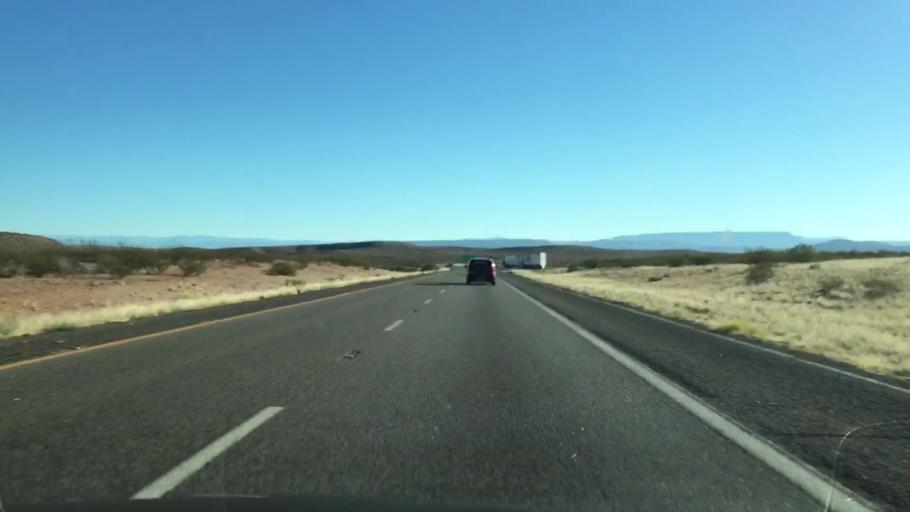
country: US
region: Utah
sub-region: Washington County
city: Saint George
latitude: 36.9864
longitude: -113.6329
